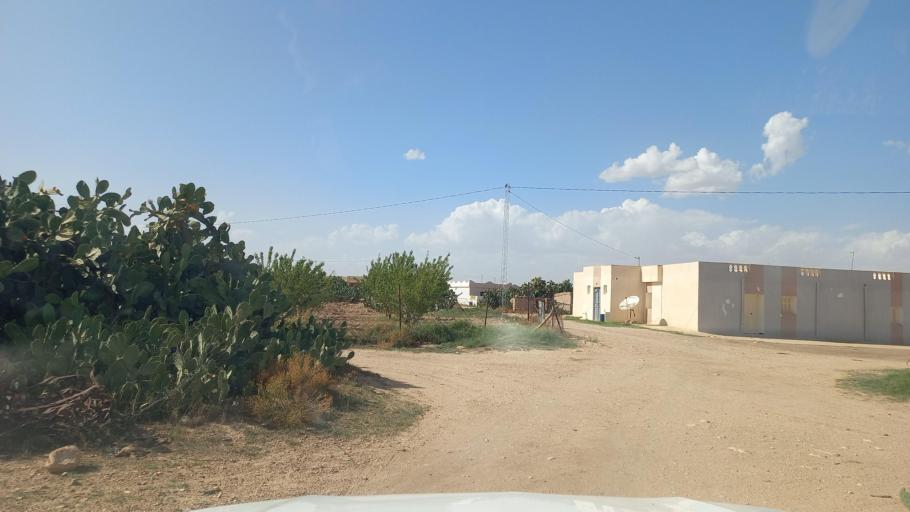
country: TN
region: Al Qasrayn
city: Sbiba
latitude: 35.3036
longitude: 9.0411
